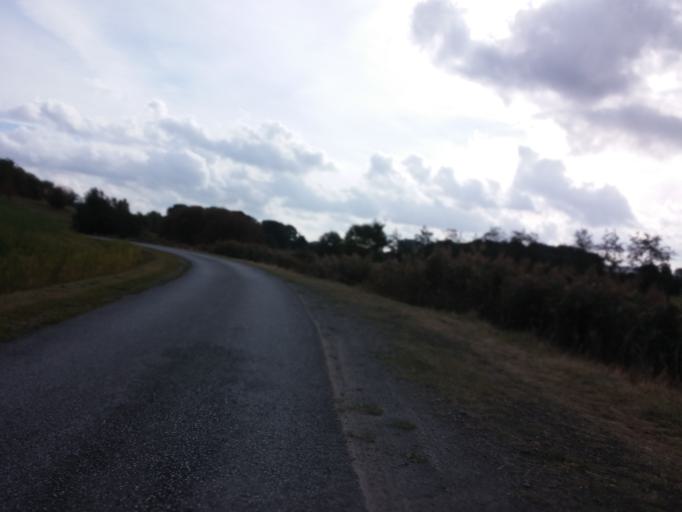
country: DE
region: North Rhine-Westphalia
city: Dorsten
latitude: 51.6510
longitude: 7.0161
